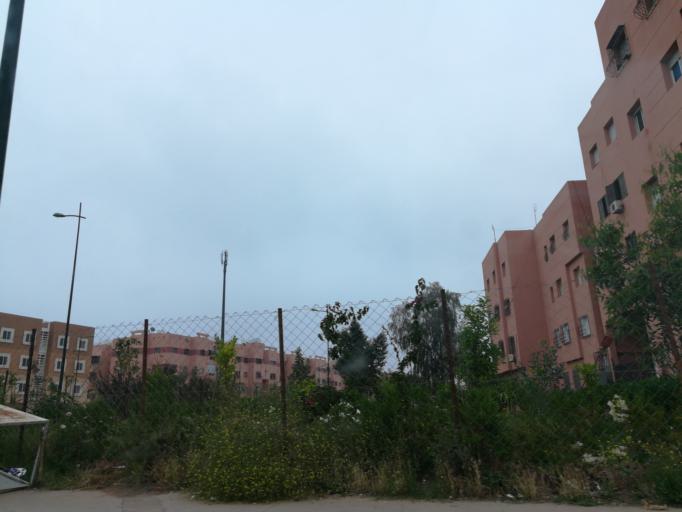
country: MA
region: Marrakech-Tensift-Al Haouz
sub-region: Marrakech
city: Marrakesh
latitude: 31.5775
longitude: -8.0609
